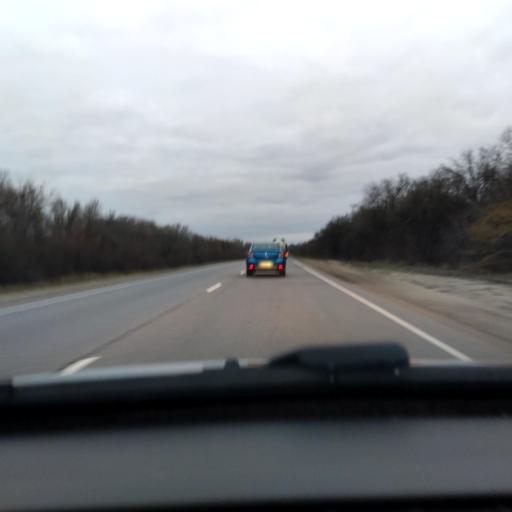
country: RU
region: Lipetsk
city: Borinskoye
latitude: 52.4332
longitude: 39.2698
